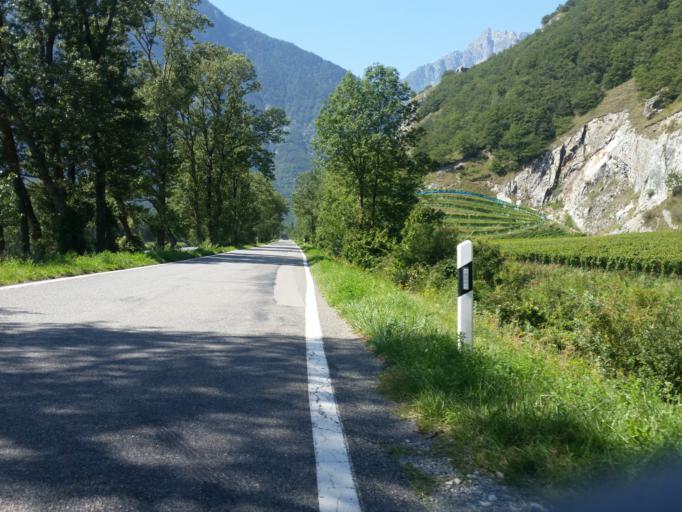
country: CH
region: Valais
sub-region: Martigny District
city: Martigny-Ville
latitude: 46.1224
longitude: 7.0786
